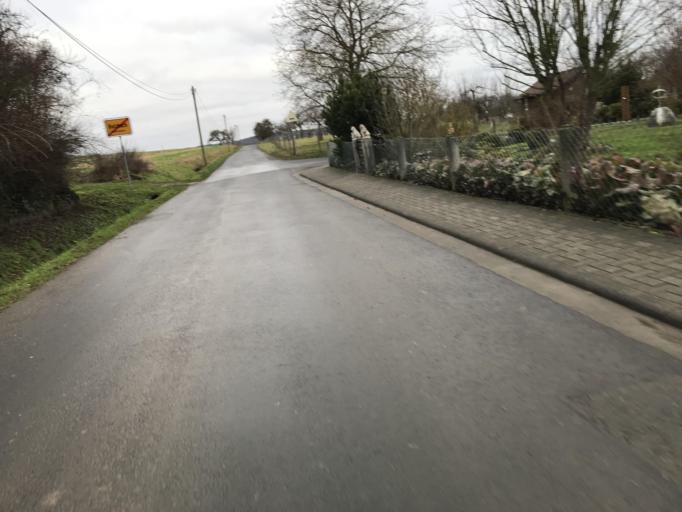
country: DE
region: Hesse
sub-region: Regierungsbezirk Giessen
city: Hoernsheim
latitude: 50.4553
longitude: 8.6066
